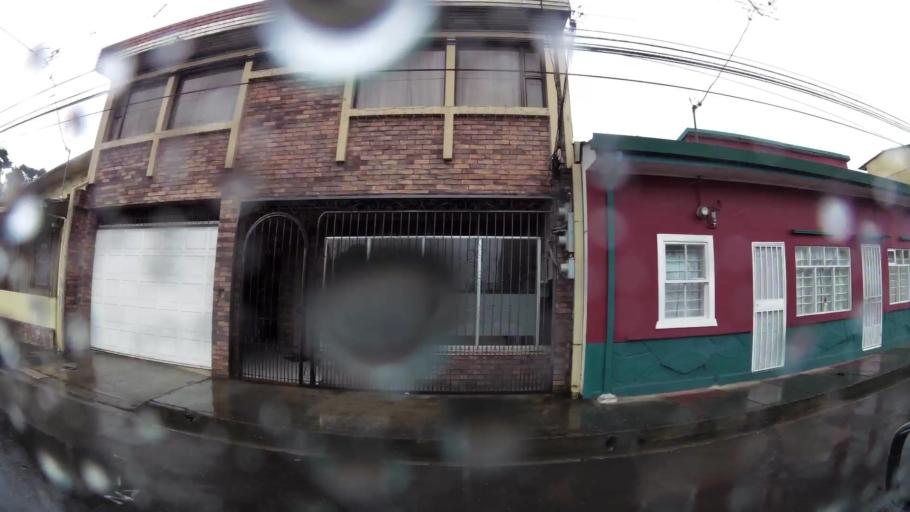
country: CR
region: Cartago
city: Cartago
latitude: 9.8644
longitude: -83.9303
